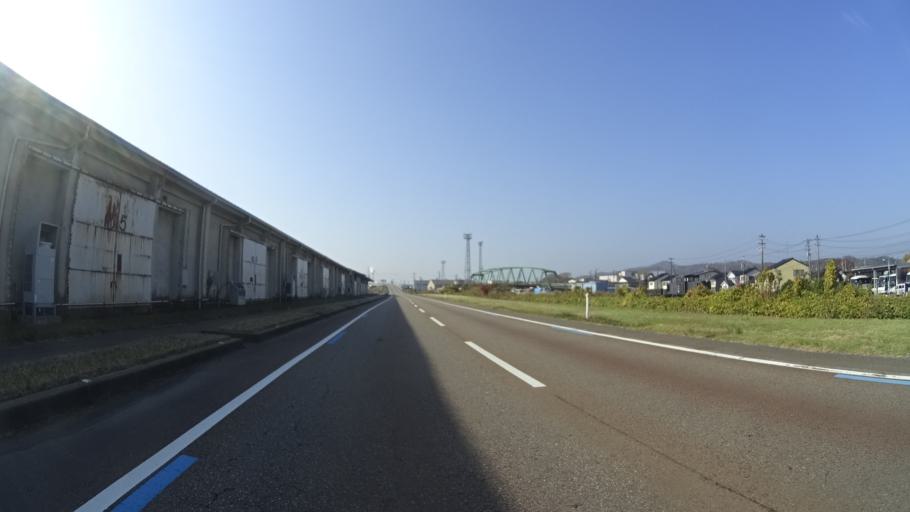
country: JP
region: Toyama
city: Nishishinminato
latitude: 36.7932
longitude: 137.0619
